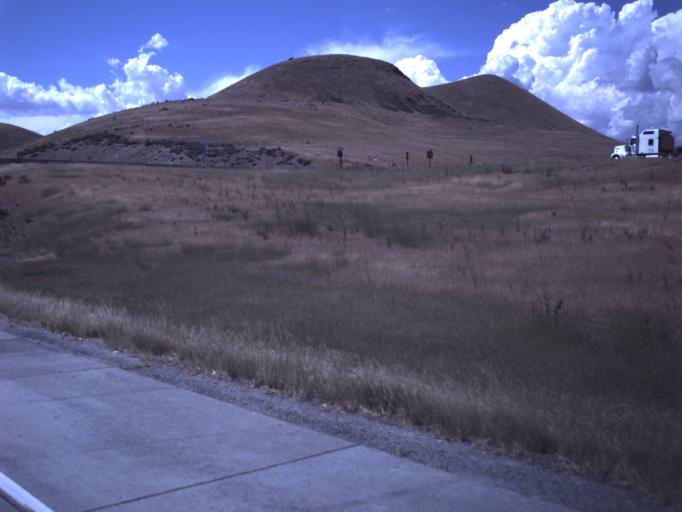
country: US
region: Utah
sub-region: Box Elder County
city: Garland
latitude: 41.7996
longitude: -112.3032
